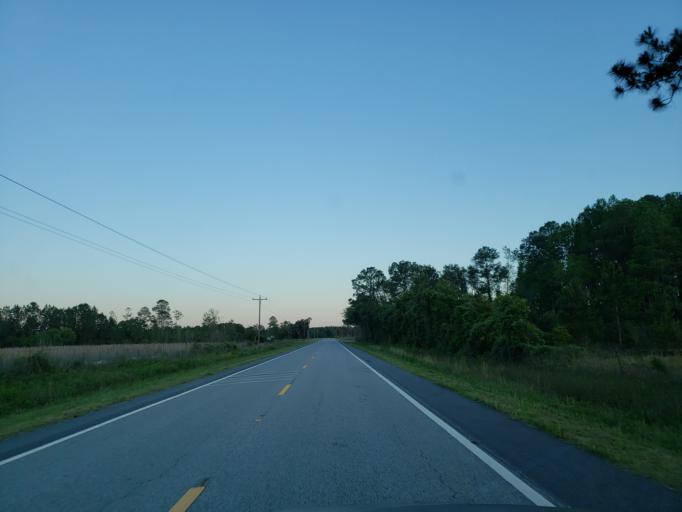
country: US
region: Georgia
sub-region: Echols County
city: Statenville
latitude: 30.5676
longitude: -83.1574
